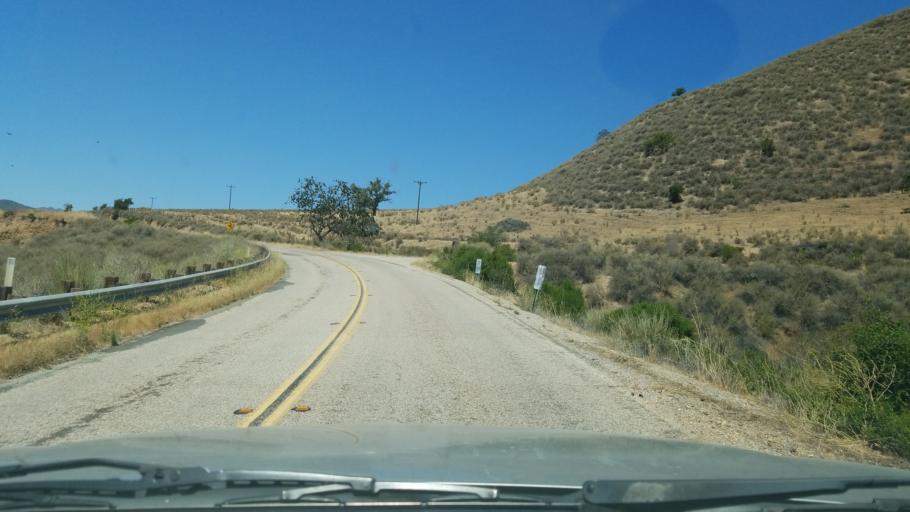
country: US
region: California
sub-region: Monterey County
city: Greenfield
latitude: 36.2719
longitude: -121.3479
